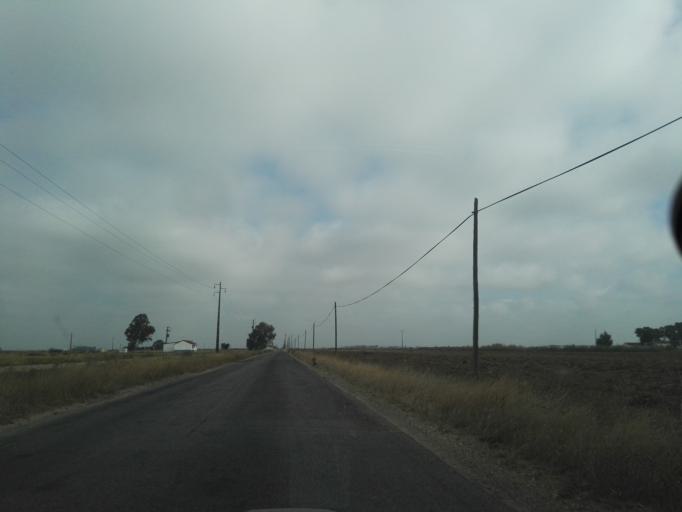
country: PT
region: Lisbon
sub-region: Vila Franca de Xira
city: Vila Franca de Xira
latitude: 38.9466
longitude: -8.9405
